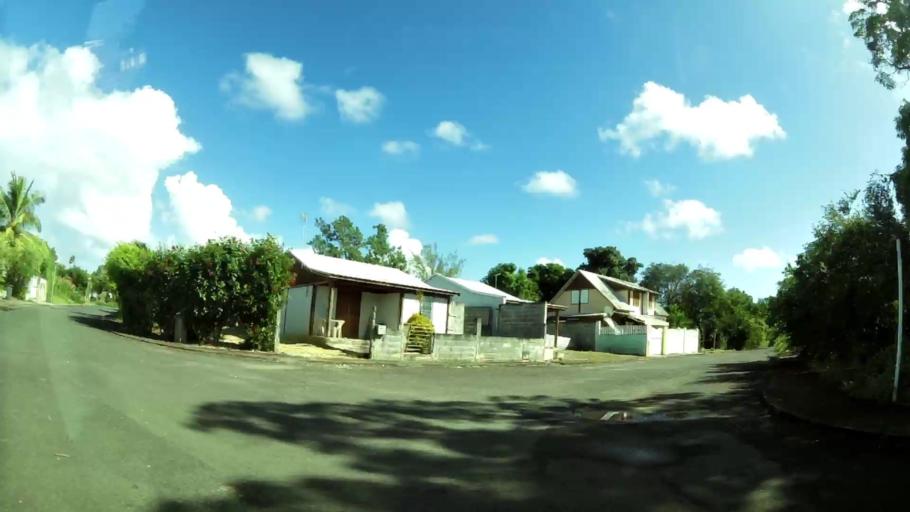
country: GP
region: Guadeloupe
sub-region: Guadeloupe
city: Port-Louis
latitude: 16.4146
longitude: -61.5276
